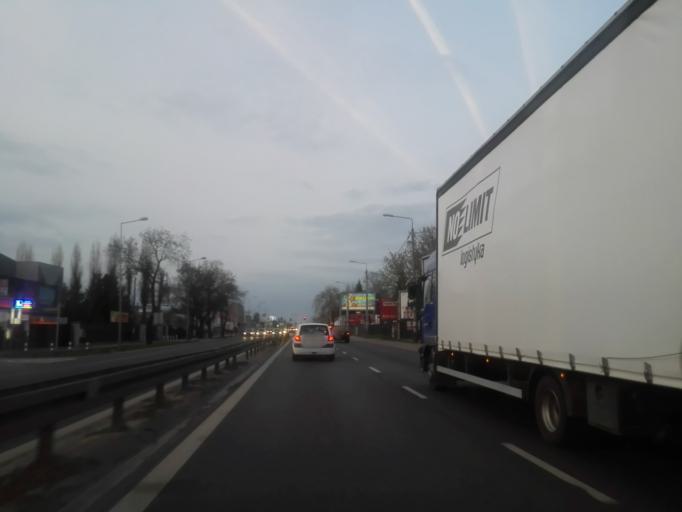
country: PL
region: Masovian Voivodeship
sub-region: Powiat pruszkowski
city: Raszyn
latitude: 52.1572
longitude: 20.9237
